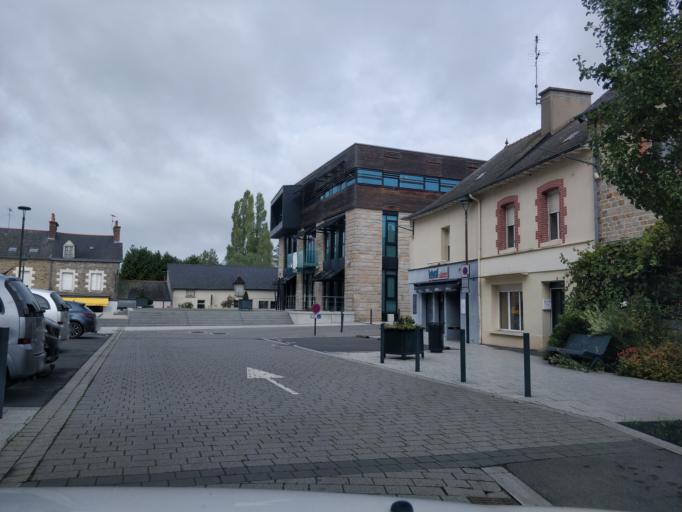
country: FR
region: Brittany
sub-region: Departement d'Ille-et-Vilaine
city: Servon-sur-Vilaine
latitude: 48.1214
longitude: -1.4598
